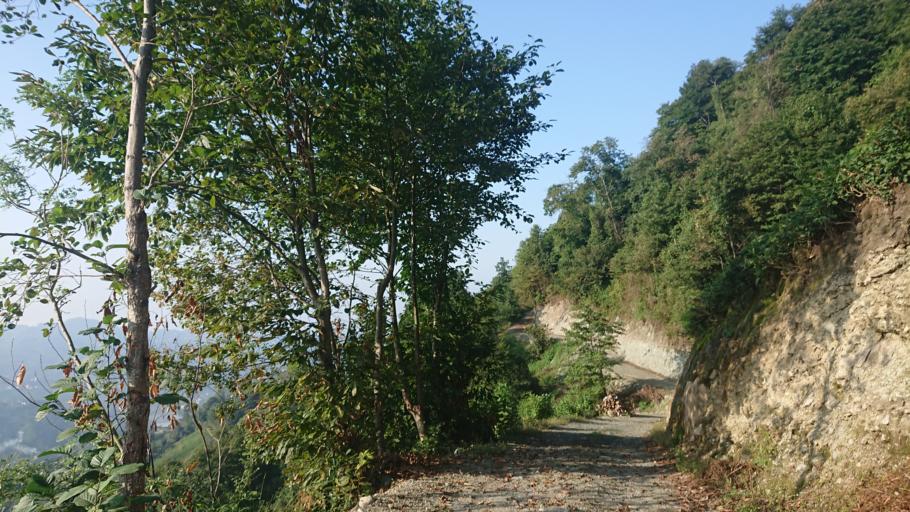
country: TR
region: Rize
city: Rize
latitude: 40.9858
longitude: 40.4983
